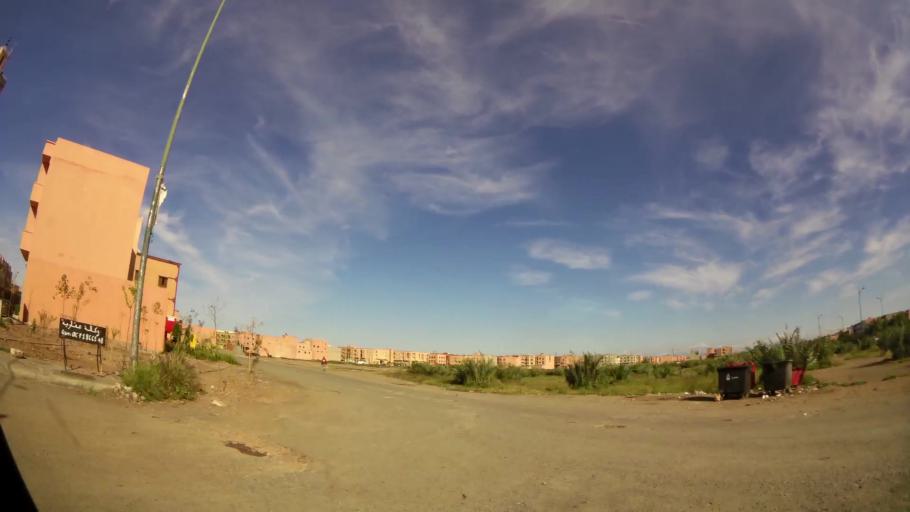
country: MA
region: Marrakech-Tensift-Al Haouz
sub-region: Marrakech
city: Marrakesh
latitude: 31.6782
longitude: -8.0469
